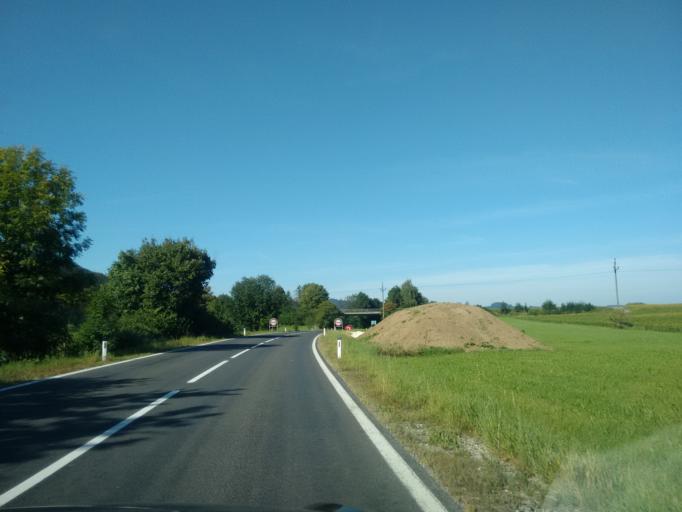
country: AT
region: Upper Austria
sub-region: Politischer Bezirk Vocklabruck
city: Seewalchen
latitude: 47.9377
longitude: 13.6049
